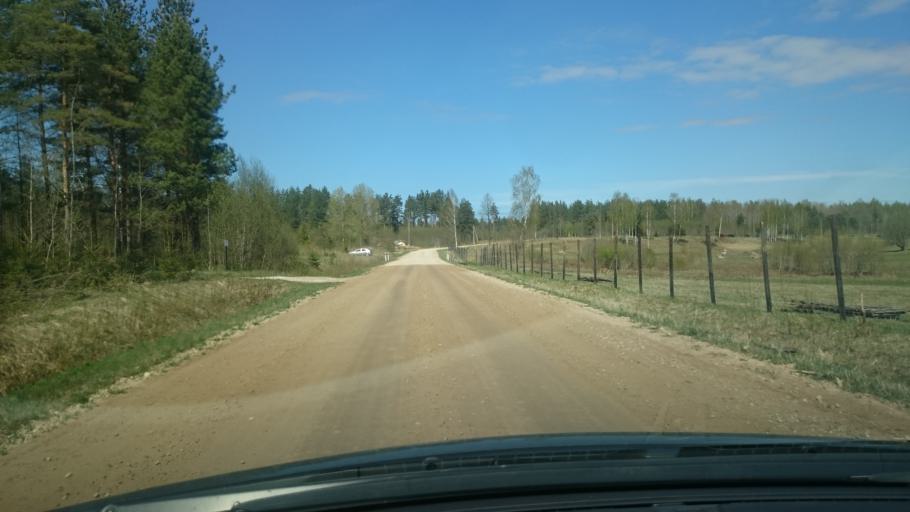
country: EE
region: Ida-Virumaa
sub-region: Sillamaee linn
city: Sillamae
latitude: 59.1265
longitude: 27.8027
